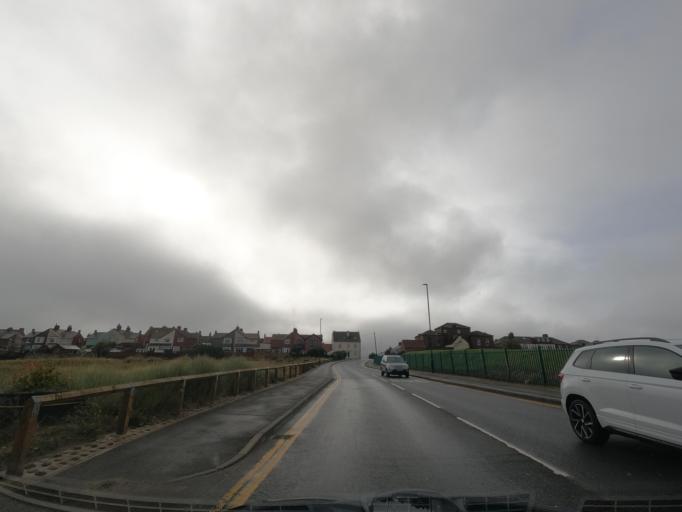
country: GB
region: England
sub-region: Redcar and Cleveland
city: Redcar
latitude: 54.6187
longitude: -1.0847
